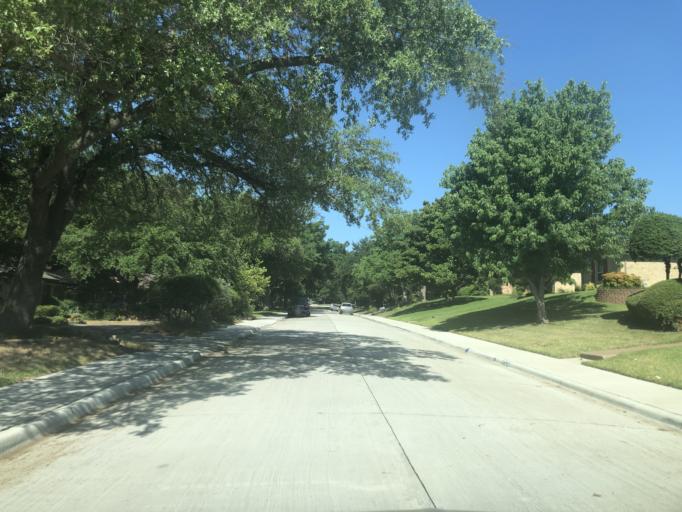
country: US
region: Texas
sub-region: Dallas County
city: Grand Prairie
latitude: 32.7541
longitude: -97.0240
